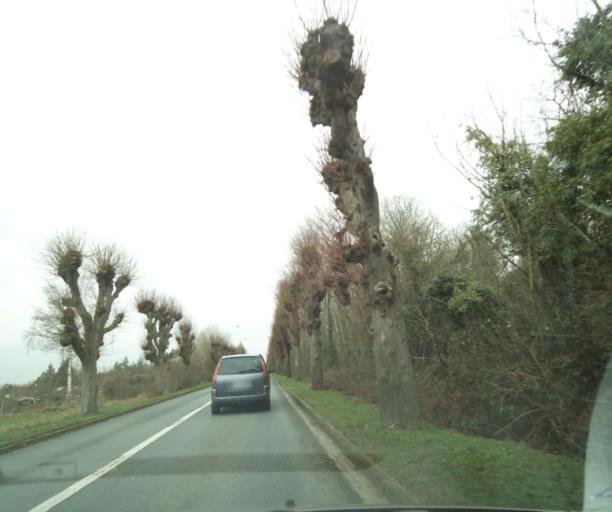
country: FR
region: Picardie
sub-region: Departement de l'Oise
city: Noyon
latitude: 49.5786
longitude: 3.0289
